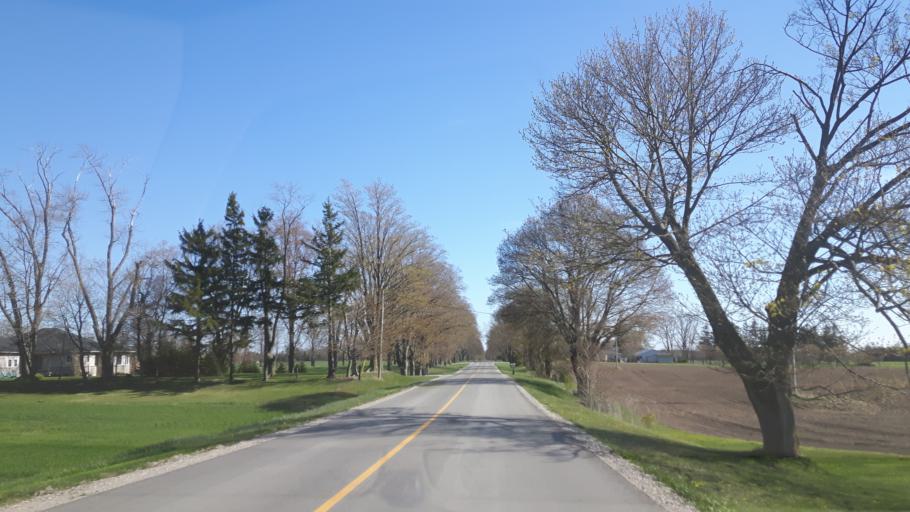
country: CA
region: Ontario
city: Goderich
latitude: 43.6264
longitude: -81.6644
